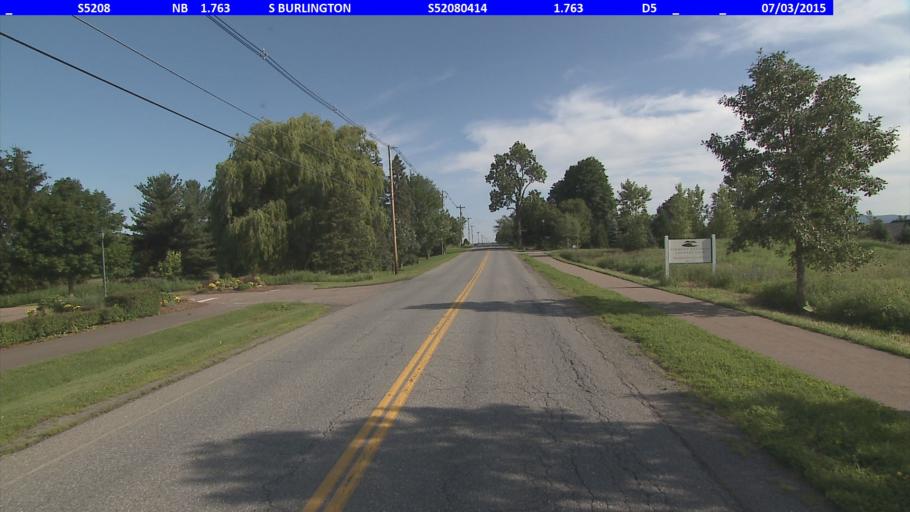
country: US
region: Vermont
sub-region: Chittenden County
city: South Burlington
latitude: 44.4359
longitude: -73.1759
